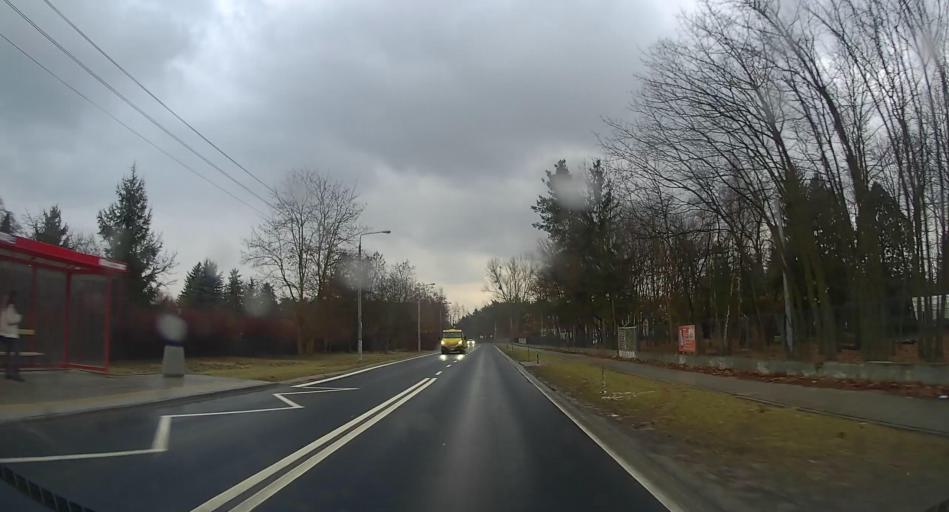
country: PL
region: Masovian Voivodeship
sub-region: Warszawa
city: Wawer
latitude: 52.1805
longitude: 21.1486
